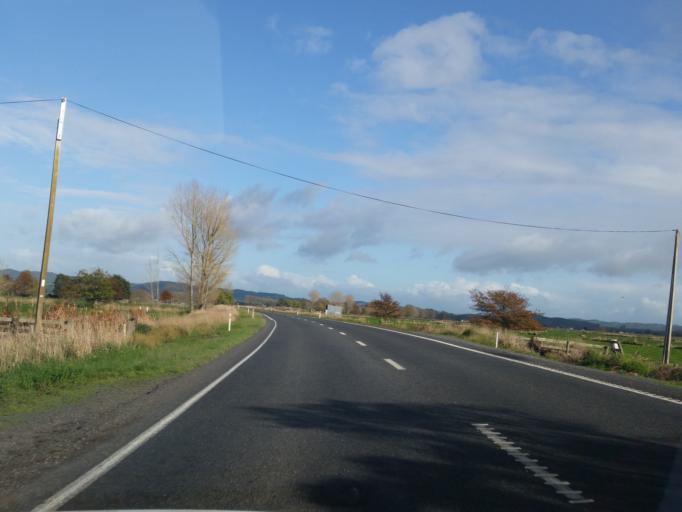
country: NZ
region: Waikato
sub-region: Hauraki District
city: Ngatea
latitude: -37.2764
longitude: 175.4634
